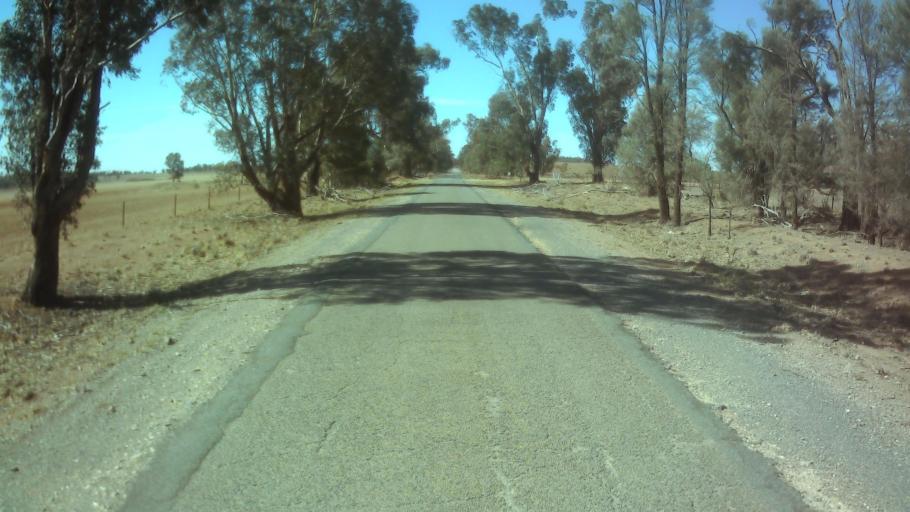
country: AU
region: New South Wales
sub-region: Forbes
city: Forbes
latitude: -33.7255
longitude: 147.7443
